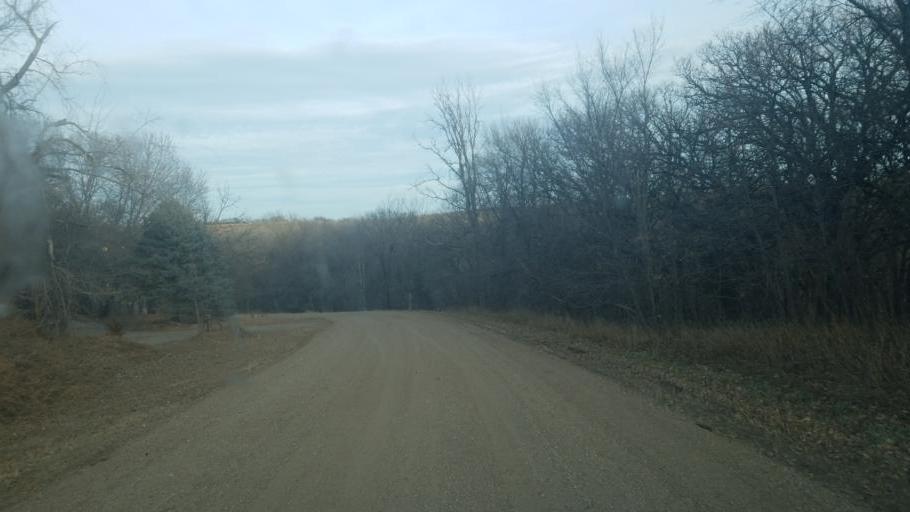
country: US
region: Nebraska
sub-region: Knox County
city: Center
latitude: 42.6855
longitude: -97.8122
